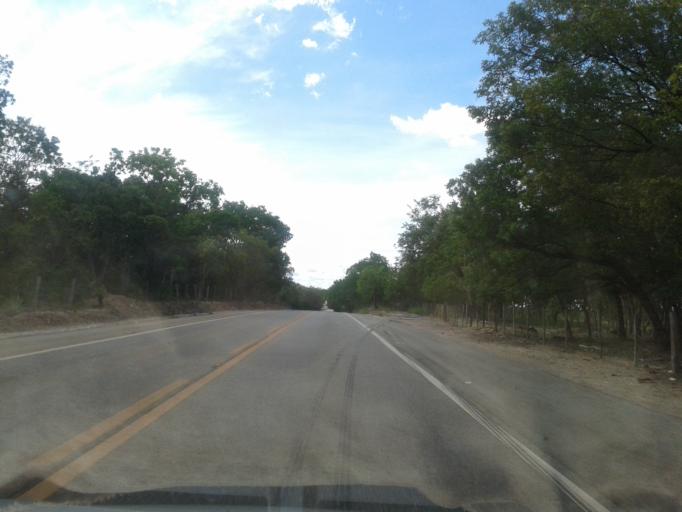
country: BR
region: Goias
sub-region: Itapuranga
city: Itapuranga
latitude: -15.4772
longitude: -50.3372
